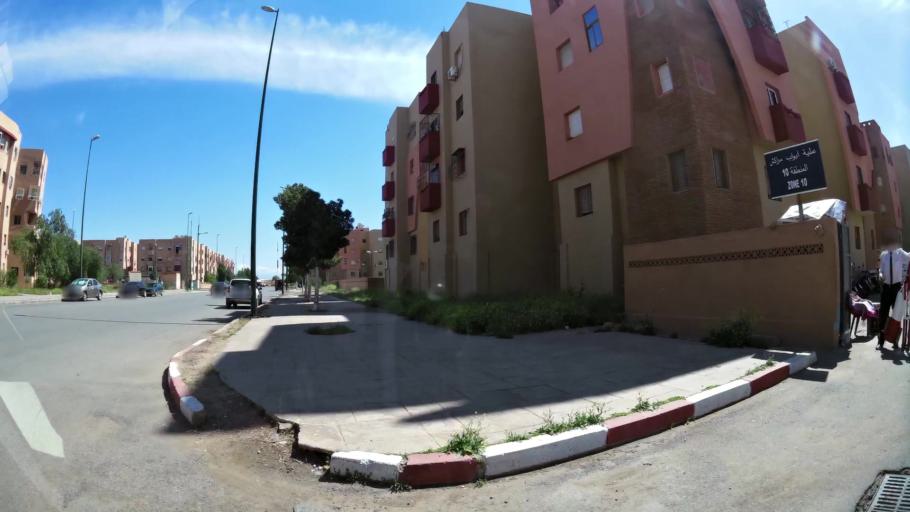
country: MA
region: Marrakech-Tensift-Al Haouz
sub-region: Marrakech
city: Marrakesh
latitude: 31.6362
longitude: -8.0780
